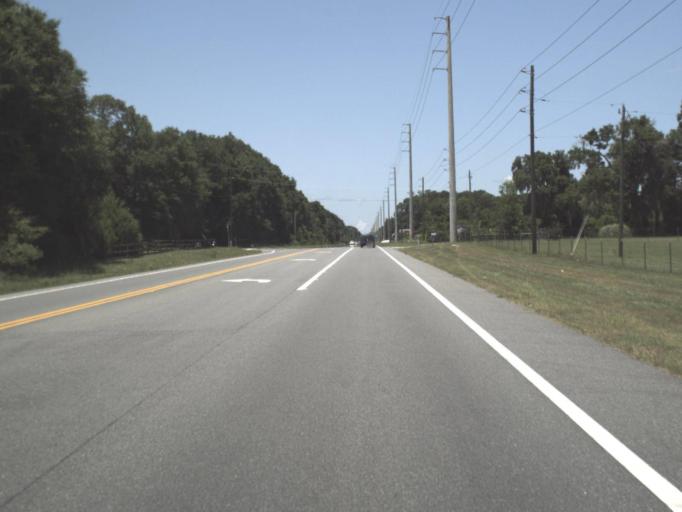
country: US
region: Florida
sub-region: Dixie County
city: Cross City
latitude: 29.6793
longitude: -82.9842
